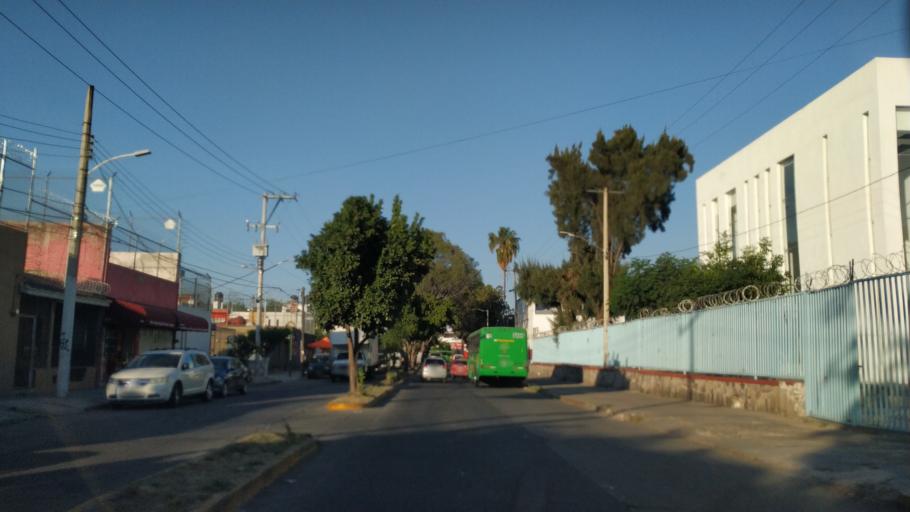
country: MX
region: Jalisco
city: Tlaquepaque
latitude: 20.6593
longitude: -103.3274
